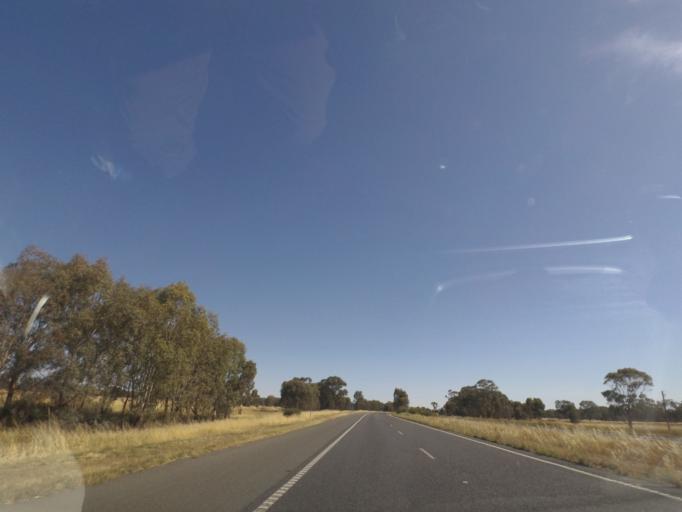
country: AU
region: Victoria
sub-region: Greater Shepparton
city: Shepparton
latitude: -36.6485
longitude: 145.2862
